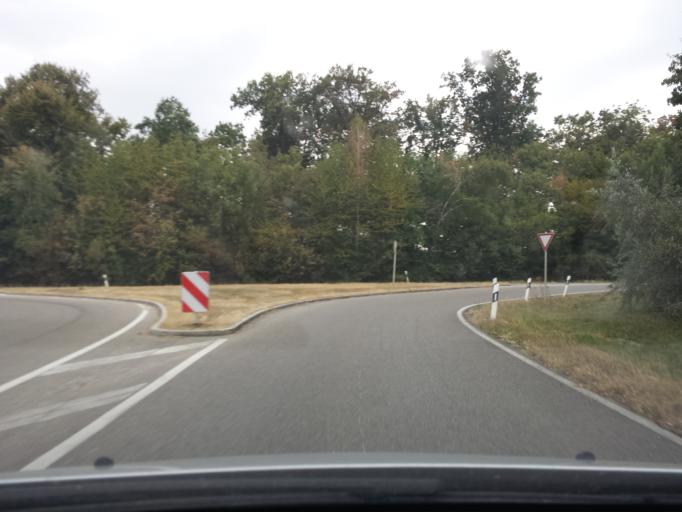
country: DE
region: Bavaria
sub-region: Swabia
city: Holzheim
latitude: 48.4069
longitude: 10.0818
